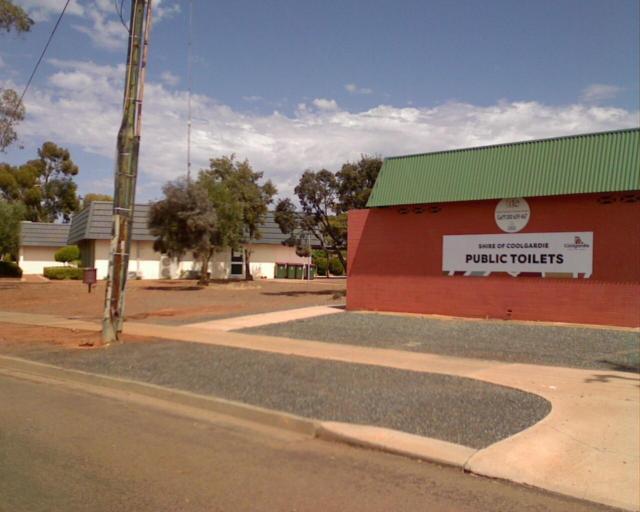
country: AU
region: Western Australia
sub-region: Kalgoorlie/Boulder
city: Stoneville
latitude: -31.2090
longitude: 121.6224
